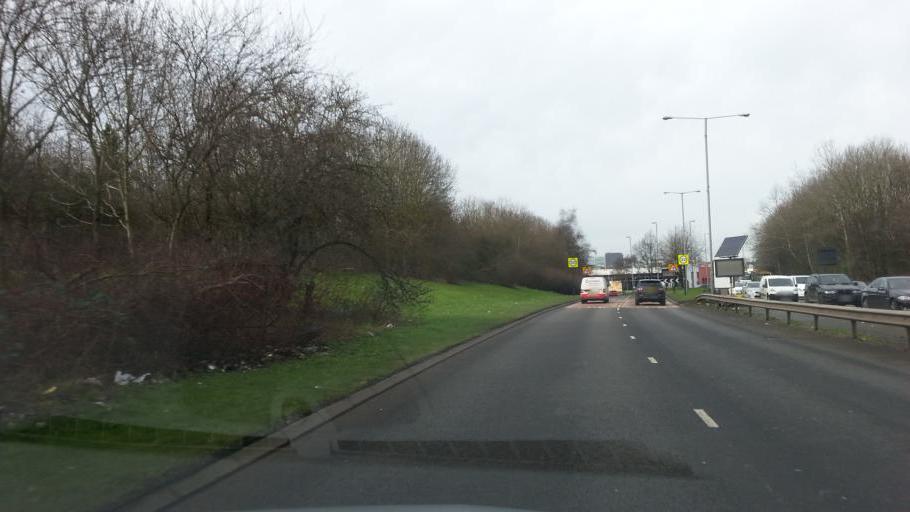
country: GB
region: England
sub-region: City and Borough of Birmingham
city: Birmingham
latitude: 52.4683
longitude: -1.8695
